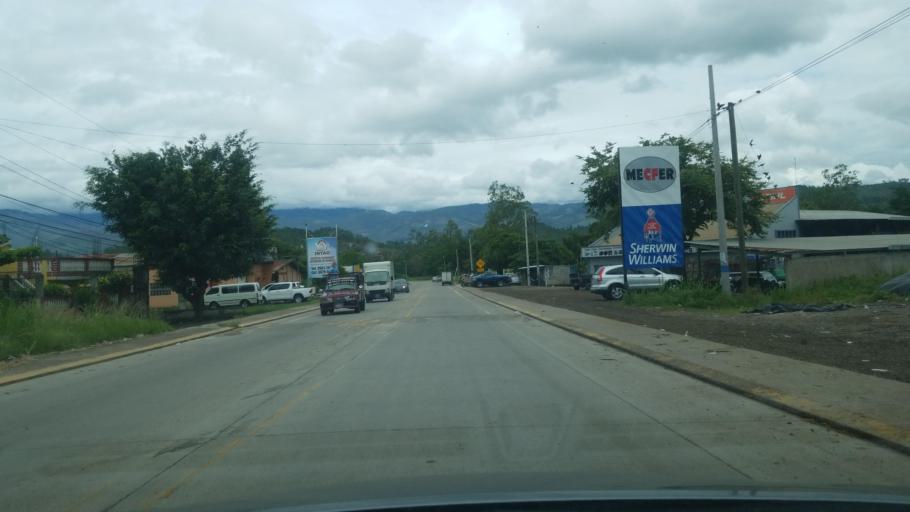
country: HN
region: Copan
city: La Entrada
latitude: 15.0685
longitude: -88.7624
